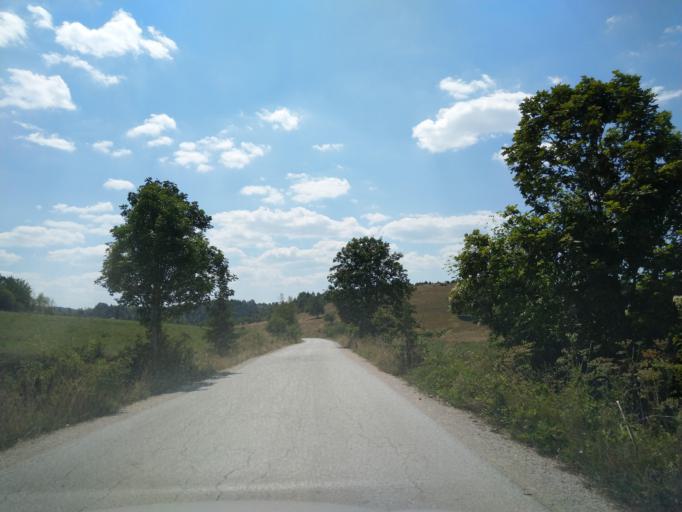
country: RS
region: Central Serbia
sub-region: Zlatiborski Okrug
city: Nova Varos
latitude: 43.4532
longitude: 19.9696
